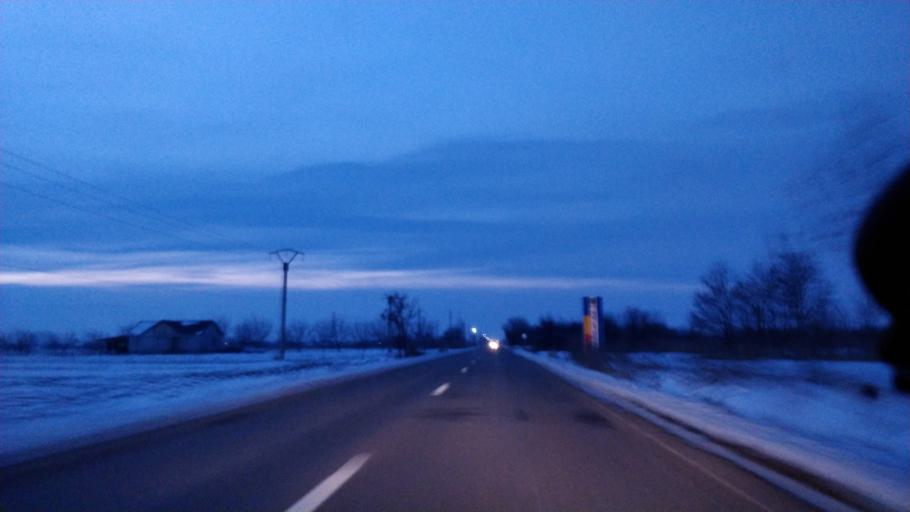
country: RO
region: Vrancea
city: Vulturu de Sus
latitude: 45.6067
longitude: 27.4478
